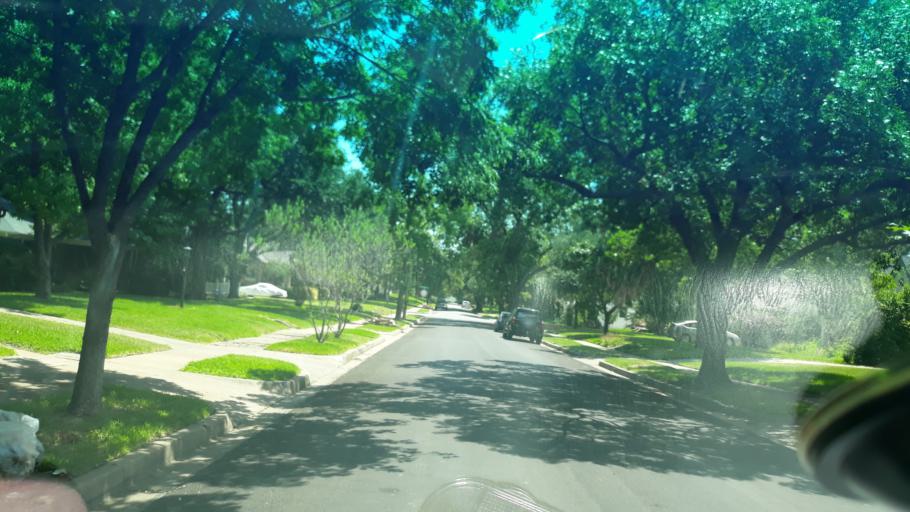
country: US
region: Texas
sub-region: Dallas County
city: Highland Park
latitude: 32.8140
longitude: -96.7389
